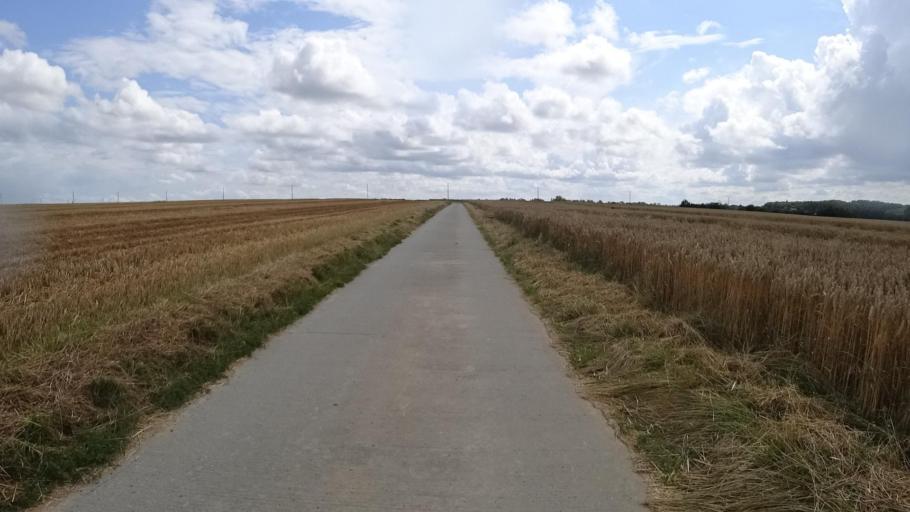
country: BE
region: Wallonia
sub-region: Province du Brabant Wallon
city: Court-Saint-Etienne
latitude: 50.5834
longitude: 4.5782
